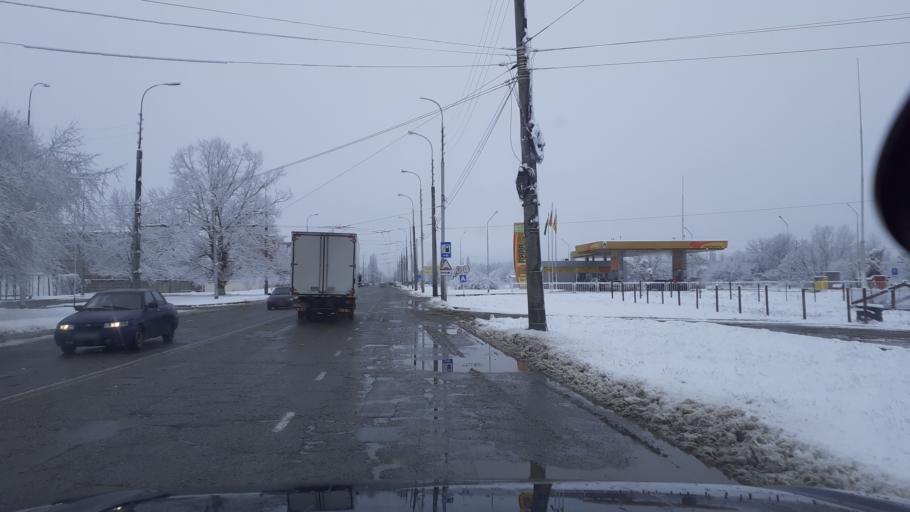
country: RU
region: Adygeya
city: Maykop
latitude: 44.6326
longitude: 40.1242
